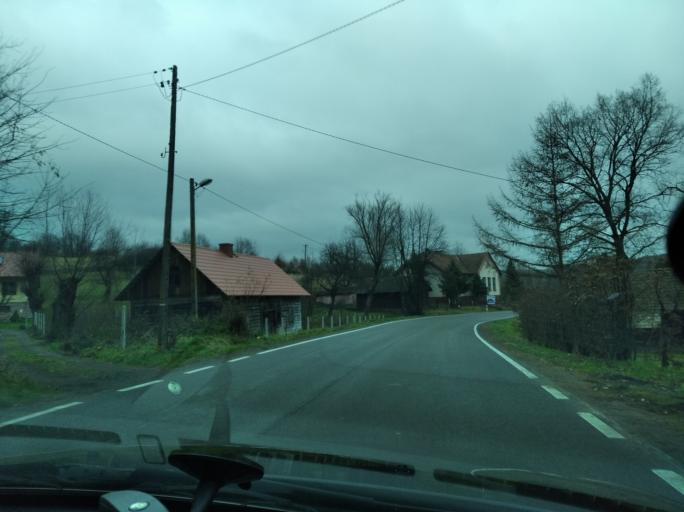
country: PL
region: Subcarpathian Voivodeship
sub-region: Powiat przeworski
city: Jawornik Polski
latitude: 49.9155
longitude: 22.3005
